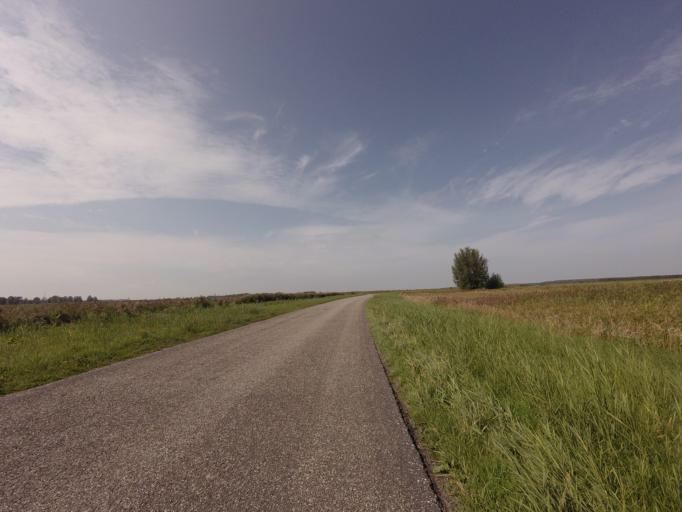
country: NL
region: Groningen
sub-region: Gemeente De Marne
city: Ulrum
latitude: 53.3467
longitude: 6.2706
